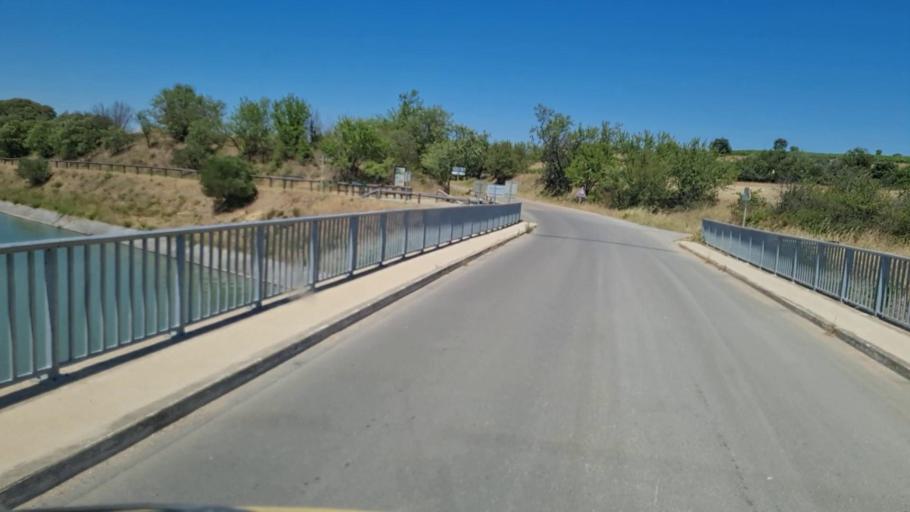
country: FR
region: Languedoc-Roussillon
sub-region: Departement du Gard
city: Vauvert
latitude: 43.6775
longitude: 4.2666
